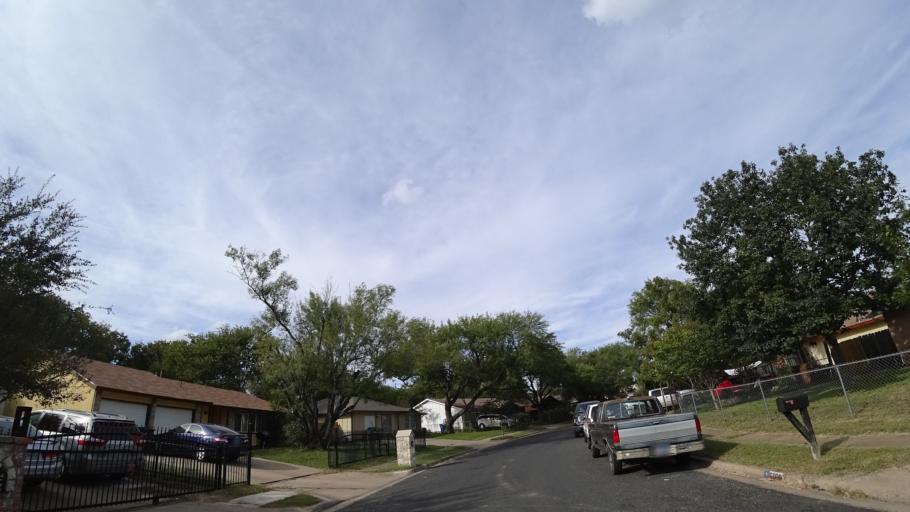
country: US
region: Texas
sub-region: Travis County
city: Austin
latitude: 30.2018
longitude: -97.7537
